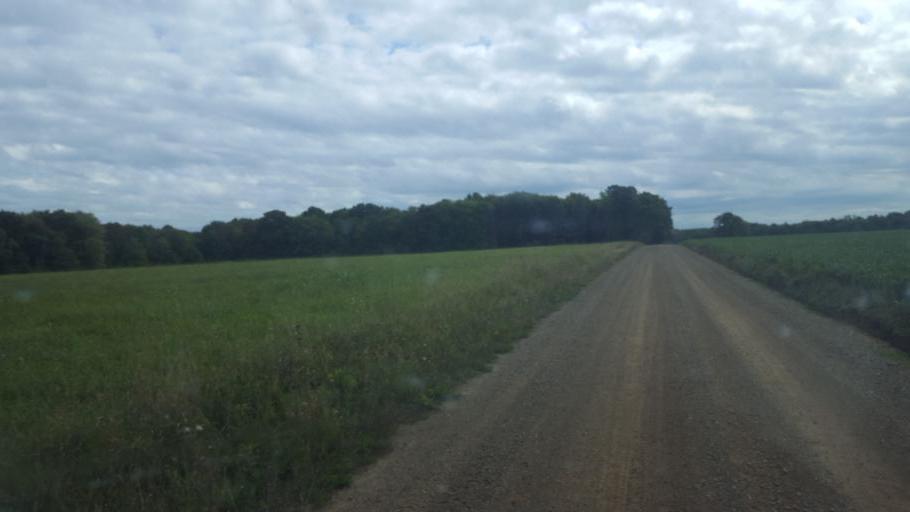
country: US
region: Pennsylvania
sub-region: Crawford County
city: Pymatuning Central
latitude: 41.5266
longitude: -80.4127
